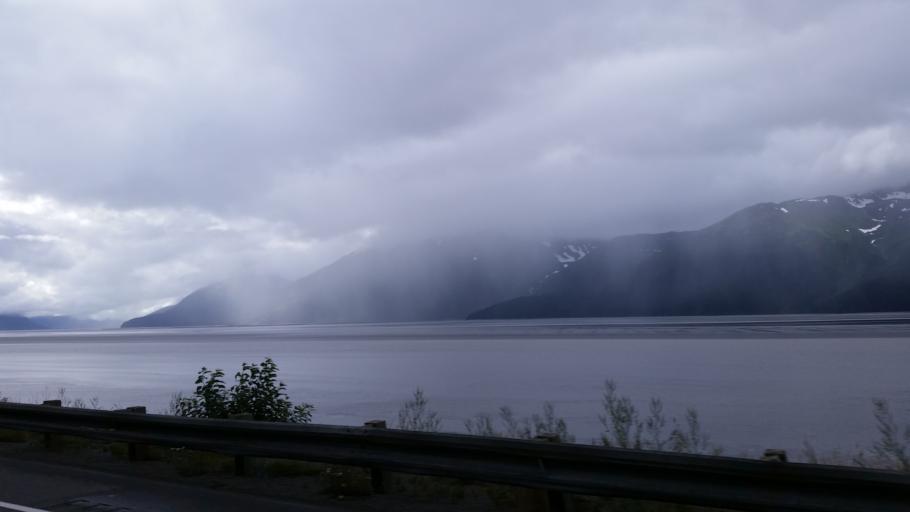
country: US
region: Alaska
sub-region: Anchorage Municipality
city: Girdwood
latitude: 60.9348
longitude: -149.3046
